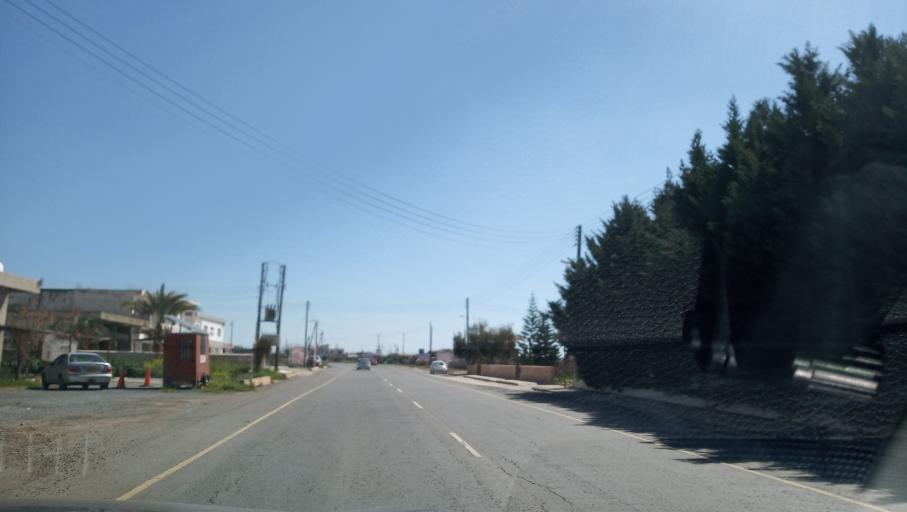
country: CY
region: Lefkosia
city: Astromeritis
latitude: 35.1367
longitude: 33.0561
